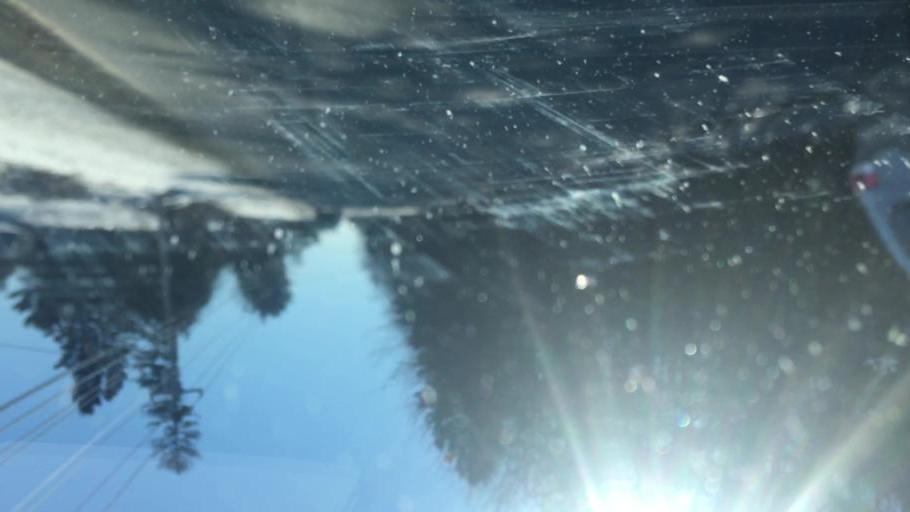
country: US
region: Maine
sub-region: Hancock County
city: Ellsworth
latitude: 44.5182
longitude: -68.4322
